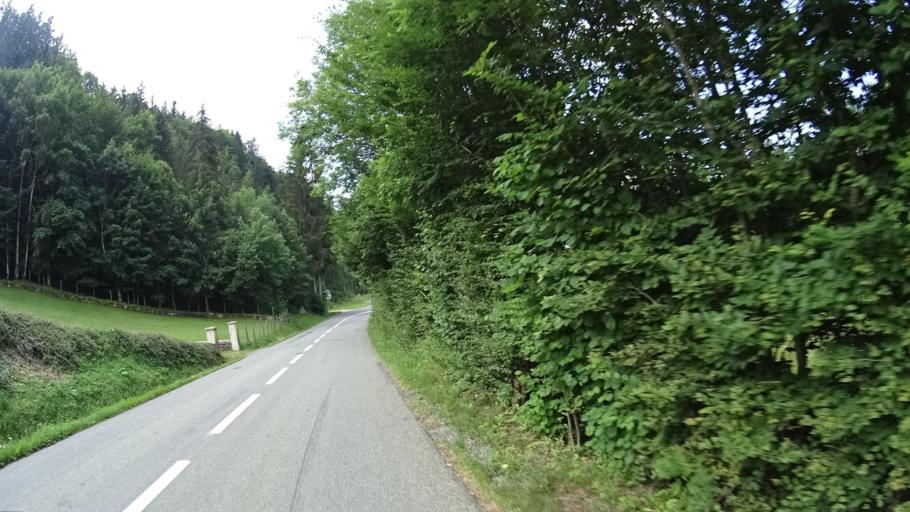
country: FR
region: Franche-Comte
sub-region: Departement du Doubs
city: Les Fourgs
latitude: 46.8305
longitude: 6.3400
